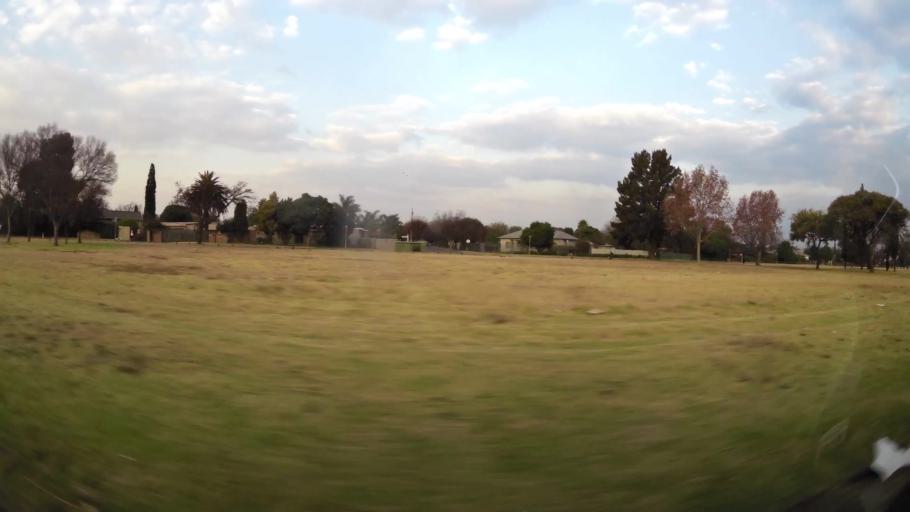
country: ZA
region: Gauteng
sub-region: Ekurhuleni Metropolitan Municipality
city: Benoni
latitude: -26.1738
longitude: 28.3105
